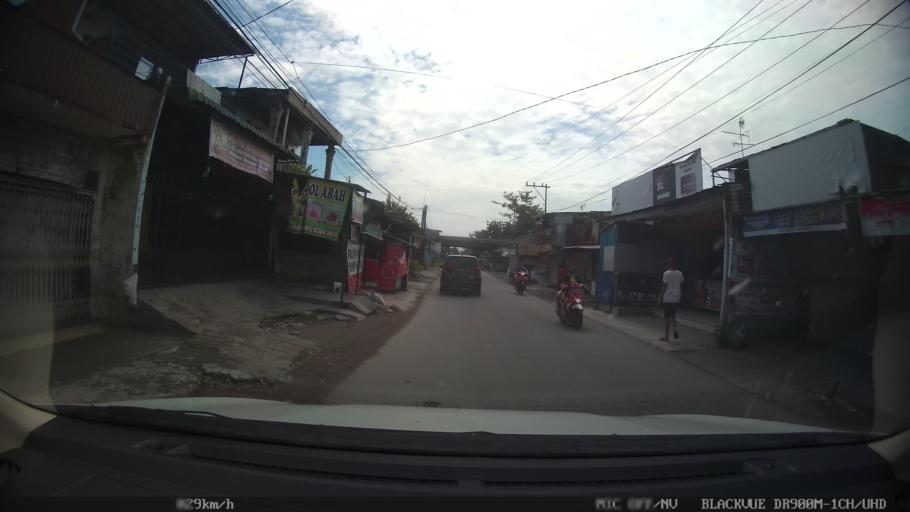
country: ID
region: North Sumatra
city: Medan
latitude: 3.5871
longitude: 98.7231
